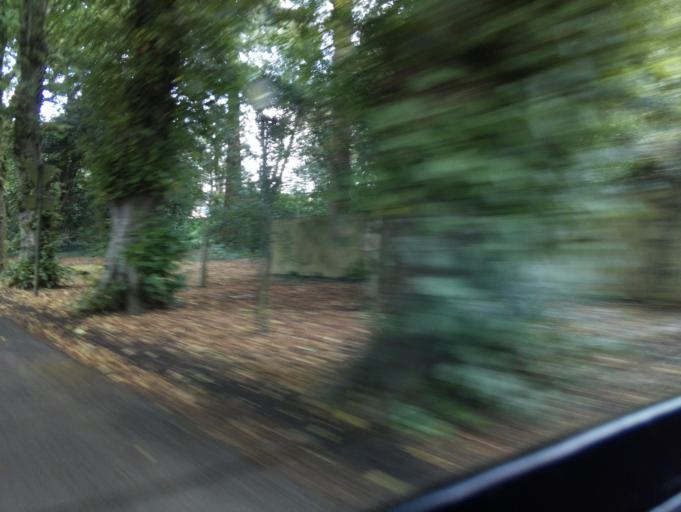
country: GB
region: England
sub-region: Staffordshire
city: Barlaston
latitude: 52.9472
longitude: -2.1577
